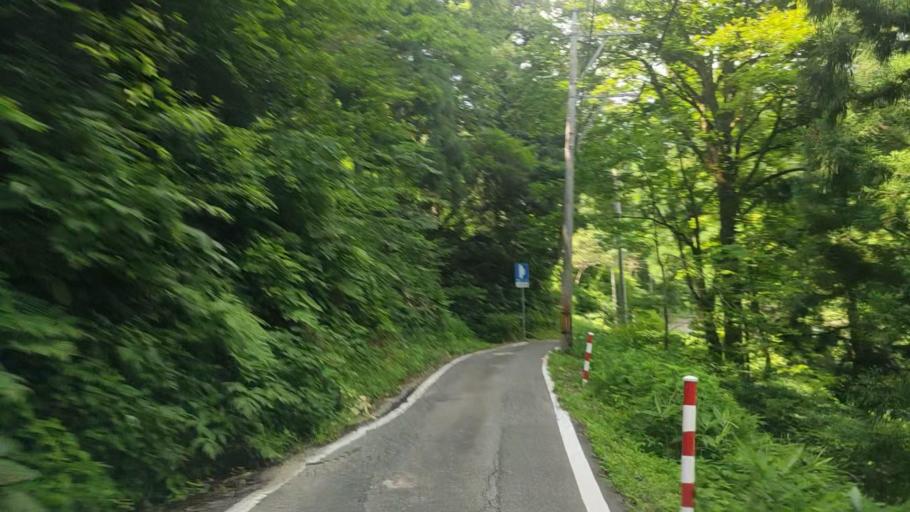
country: JP
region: Fukui
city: Katsuyama
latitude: 36.2098
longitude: 136.5277
